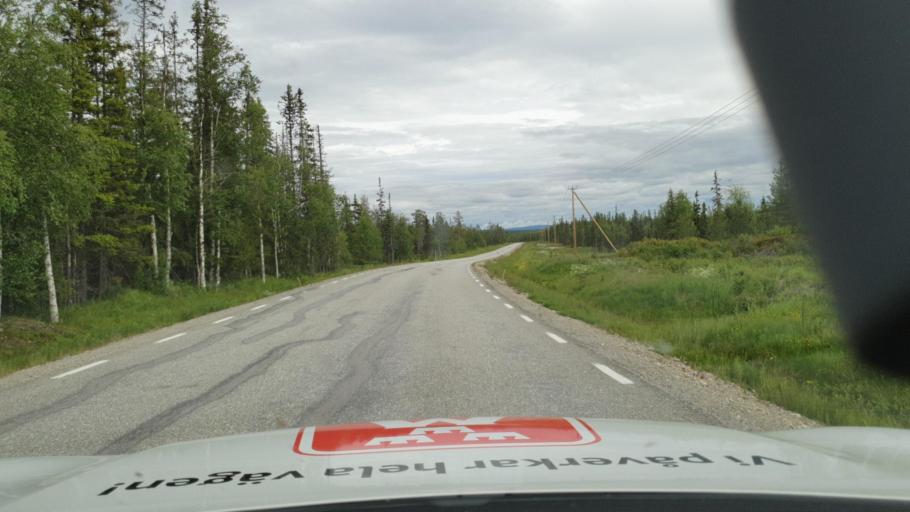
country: SE
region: Vaesterbotten
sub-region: Lycksele Kommun
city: Soderfors
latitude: 64.3782
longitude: 18.0345
